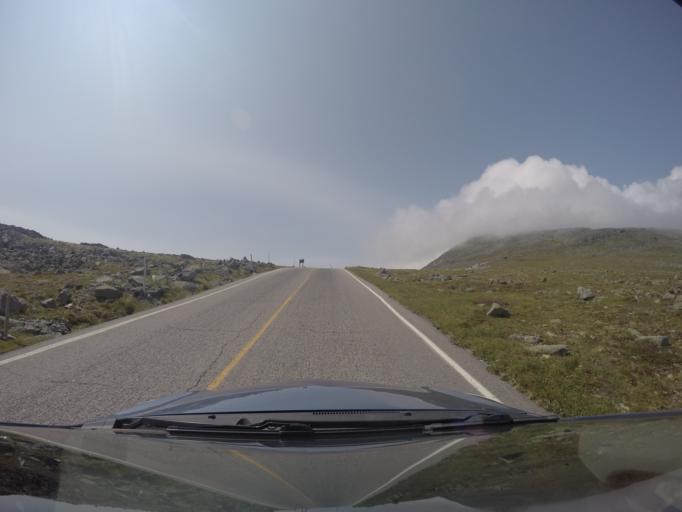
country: US
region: New Hampshire
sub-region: Coos County
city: Gorham
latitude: 44.2793
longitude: -71.2927
